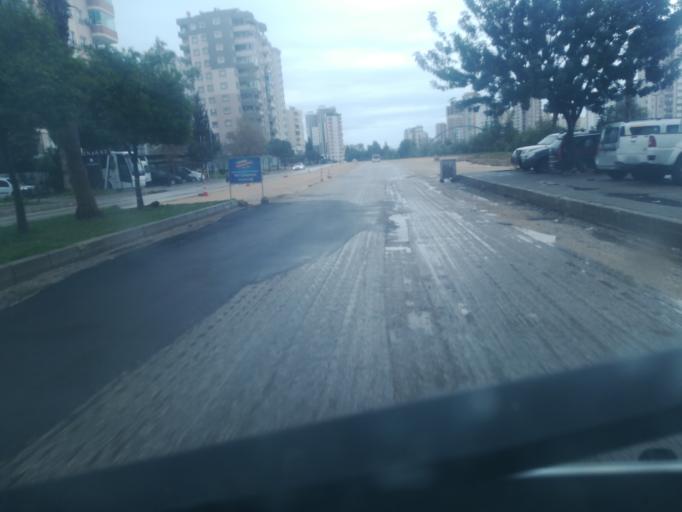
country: TR
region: Adana
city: Seyhan
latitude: 37.0318
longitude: 35.2823
